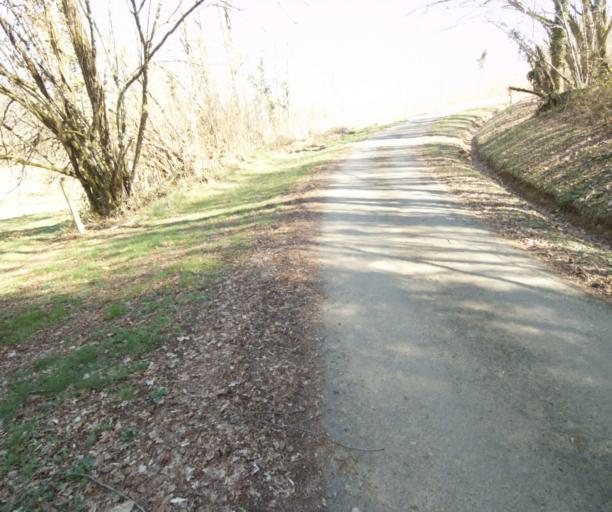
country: FR
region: Limousin
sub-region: Departement de la Correze
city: Saint-Clement
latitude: 45.3897
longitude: 1.6639
